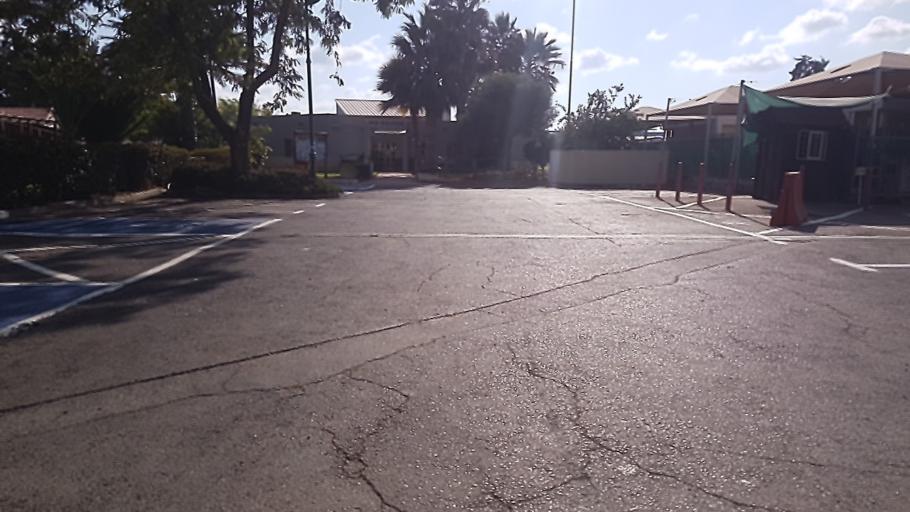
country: IL
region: Central District
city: Jaljulya
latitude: 32.1721
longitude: 34.9400
